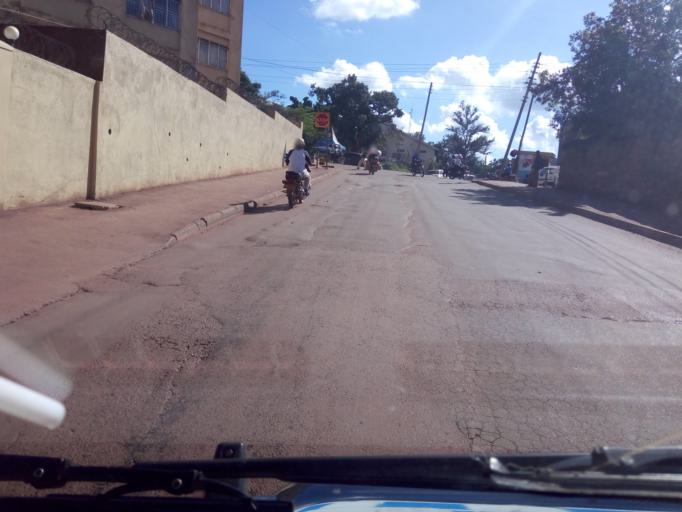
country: UG
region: Central Region
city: Kampala Central Division
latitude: 0.3183
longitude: 32.5686
